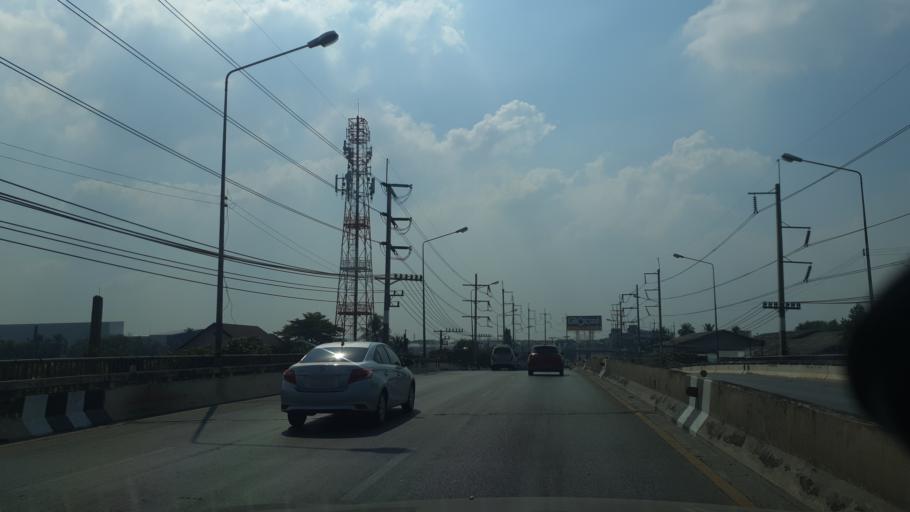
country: TH
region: Samut Sakhon
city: Krathum Baen
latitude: 13.6587
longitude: 100.2742
